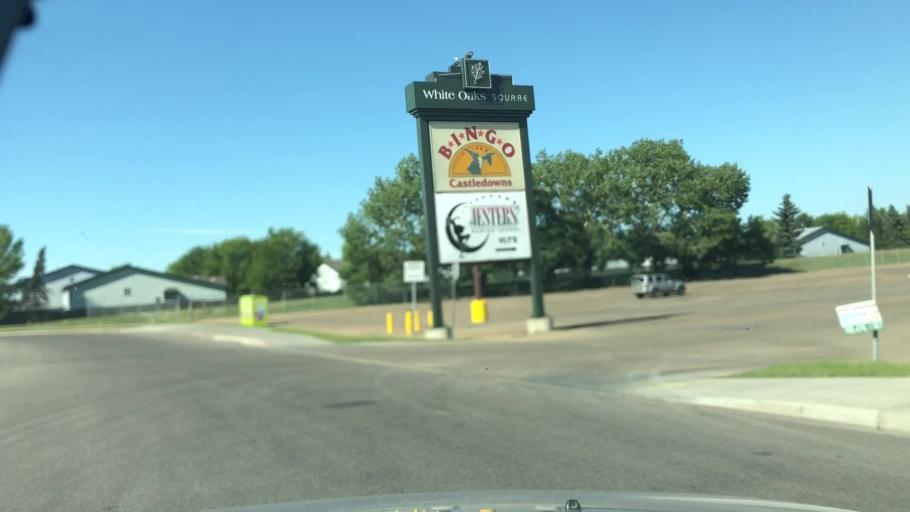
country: CA
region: Alberta
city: Edmonton
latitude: 53.6010
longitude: -113.5351
